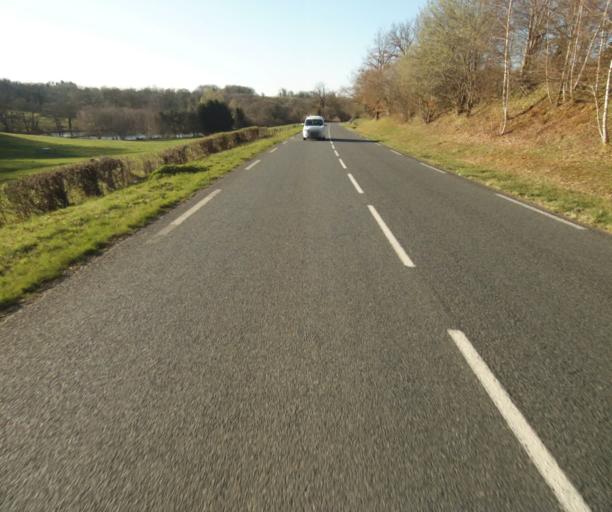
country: FR
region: Limousin
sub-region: Departement de la Correze
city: Seilhac
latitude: 45.3914
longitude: 1.7195
